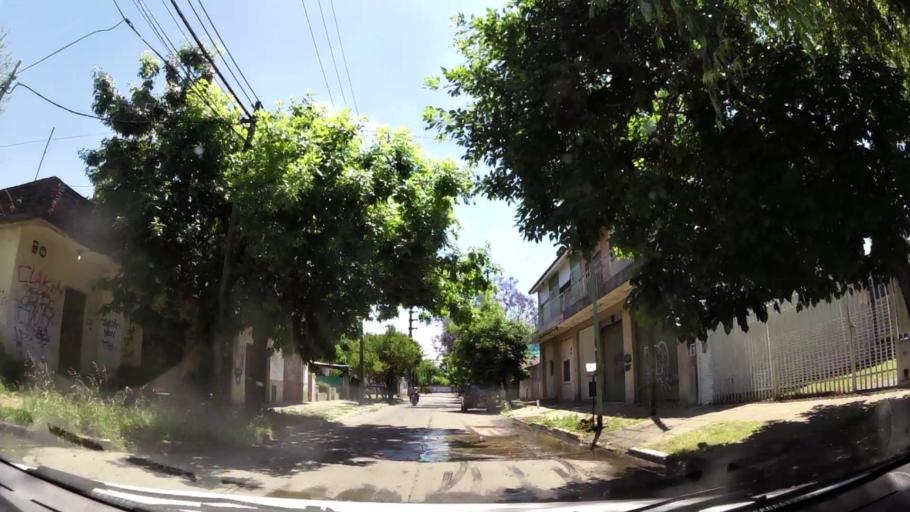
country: AR
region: Buenos Aires
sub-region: Partido de Merlo
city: Merlo
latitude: -34.6581
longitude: -58.7113
